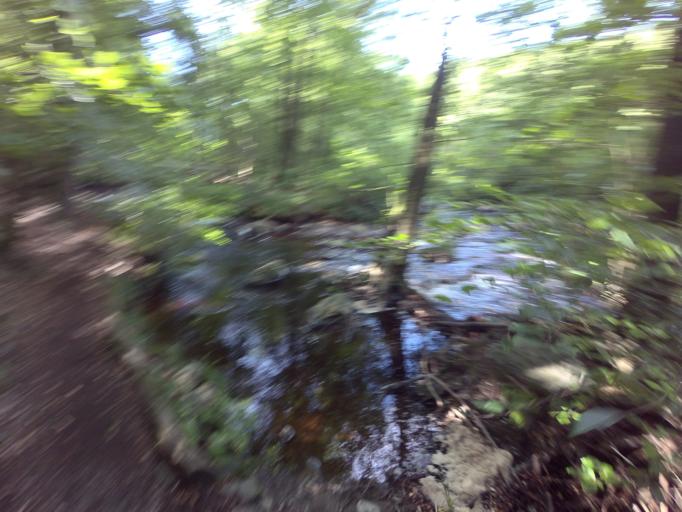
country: BE
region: Wallonia
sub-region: Province de Liege
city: Jalhay
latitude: 50.5061
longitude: 5.9623
